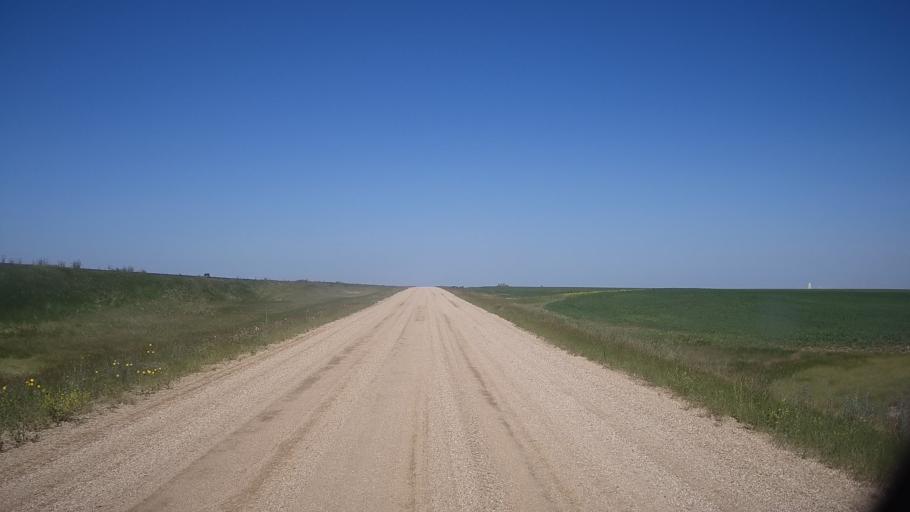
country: CA
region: Saskatchewan
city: Watrous
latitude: 51.8782
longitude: -106.0143
